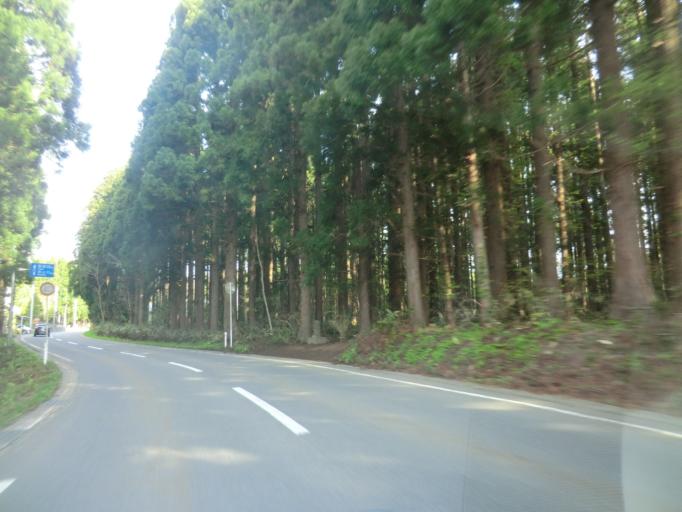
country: JP
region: Aomori
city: Mutsu
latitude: 41.3024
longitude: 141.2003
